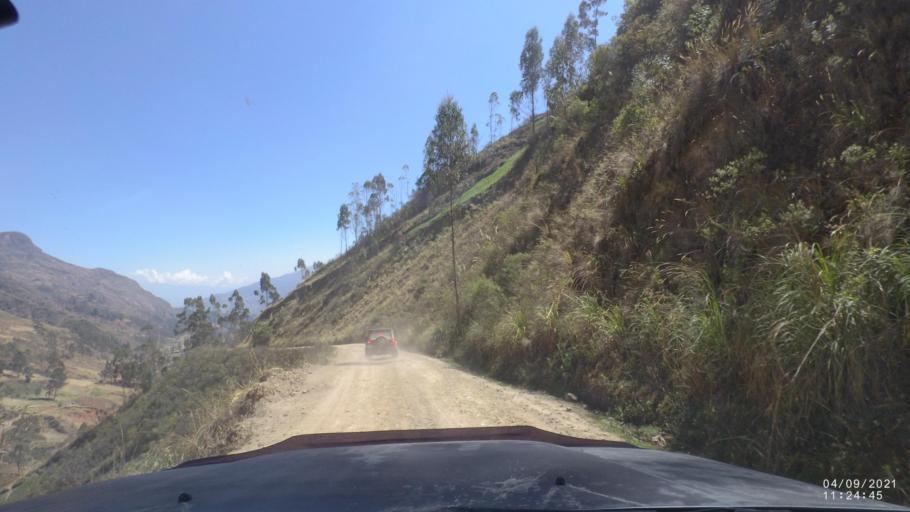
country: BO
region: Cochabamba
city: Colchani
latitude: -17.2588
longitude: -66.5099
